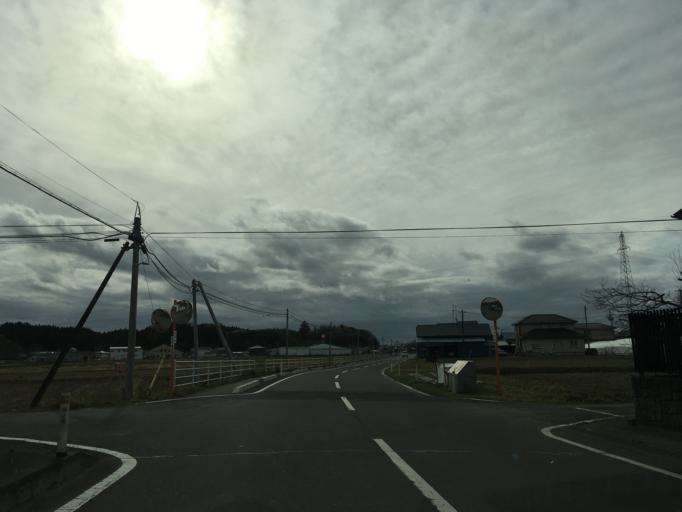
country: JP
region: Iwate
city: Ichinoseki
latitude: 38.7366
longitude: 141.2771
